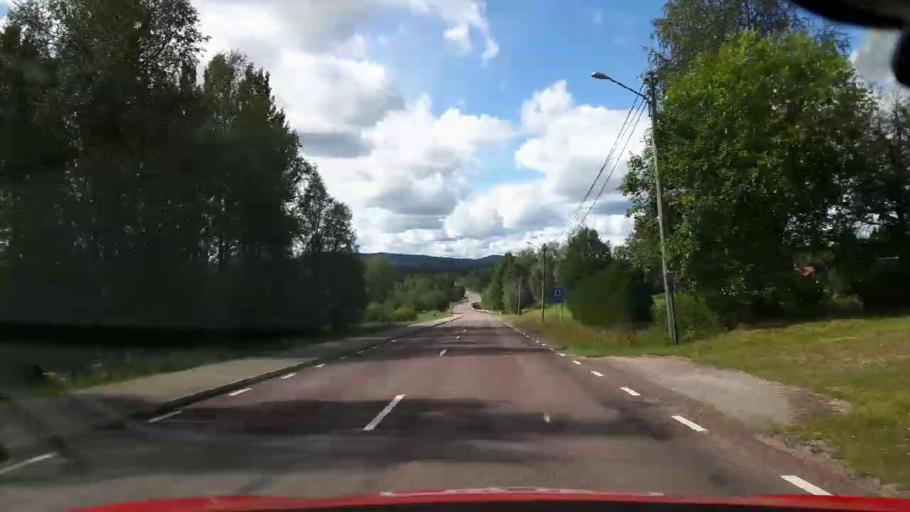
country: SE
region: Jaemtland
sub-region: Harjedalens Kommun
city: Sveg
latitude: 61.8583
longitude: 14.0983
